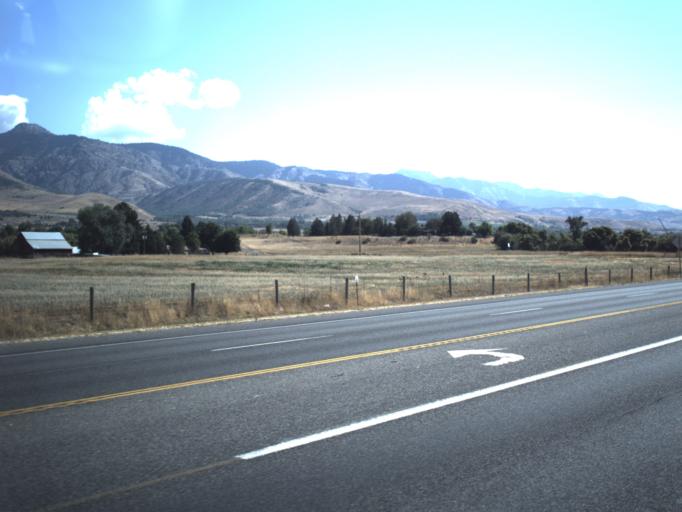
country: US
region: Utah
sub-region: Cache County
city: Richmond
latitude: 41.9606
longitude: -111.8130
